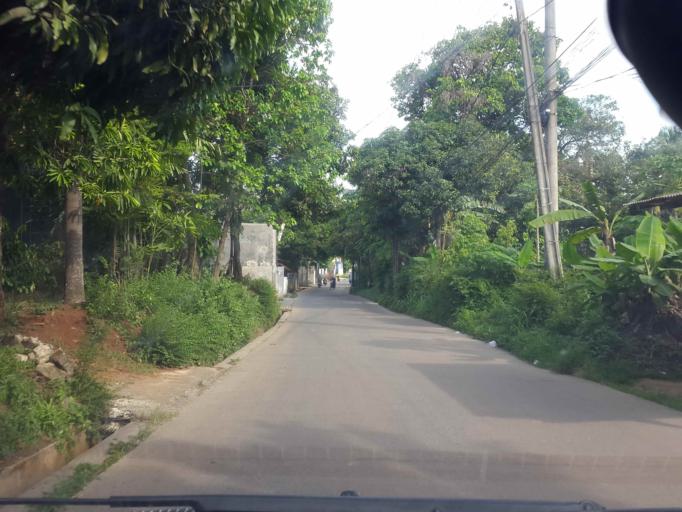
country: ID
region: West Java
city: Ciputat
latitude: -6.2550
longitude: 106.6716
